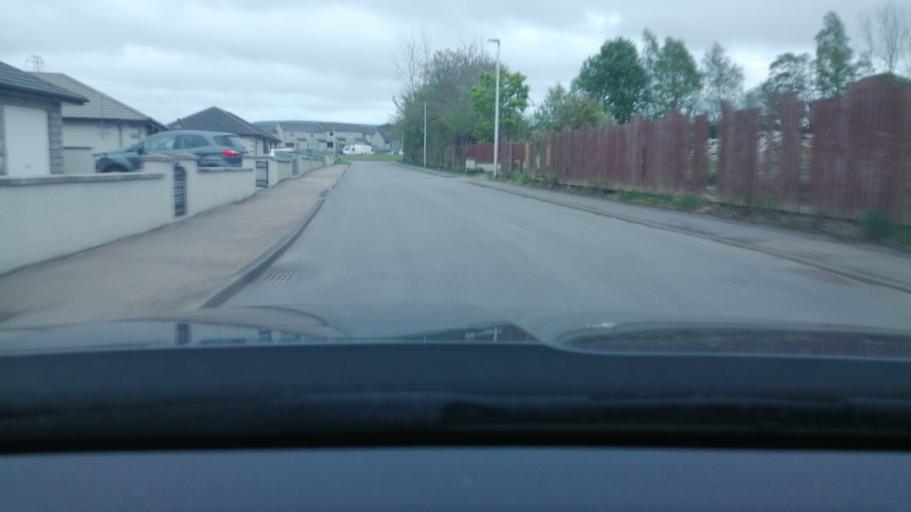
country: GB
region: Scotland
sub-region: Moray
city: Keith
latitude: 57.5363
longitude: -2.9473
